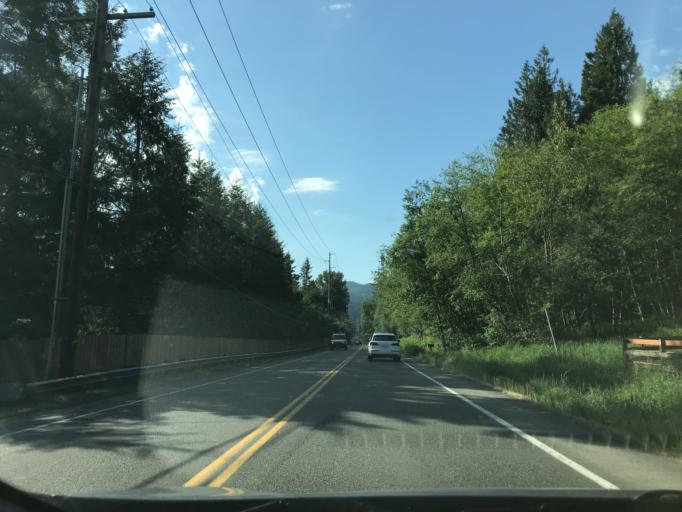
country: US
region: Washington
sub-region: King County
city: Mirrormont
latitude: 47.4682
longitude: -122.0187
